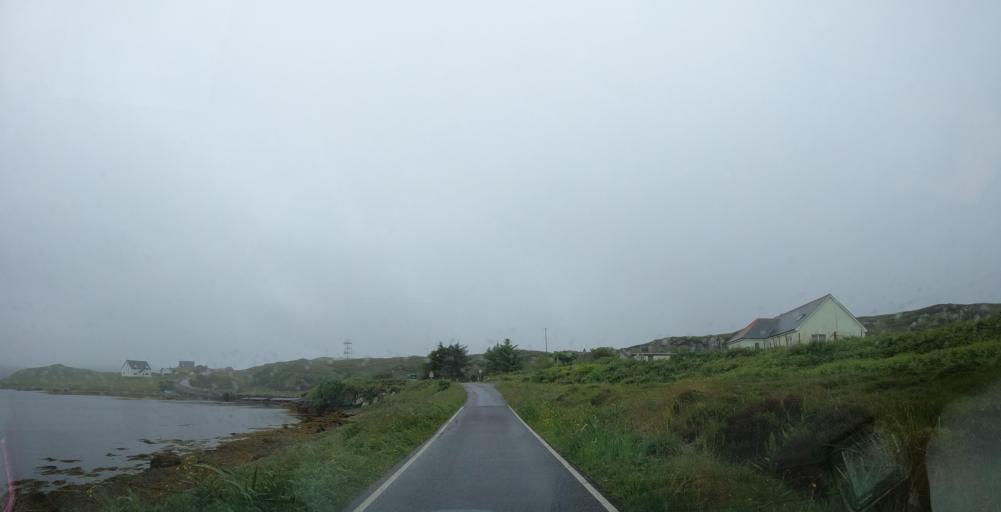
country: GB
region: Scotland
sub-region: Eilean Siar
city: Barra
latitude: 56.9911
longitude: -7.4218
